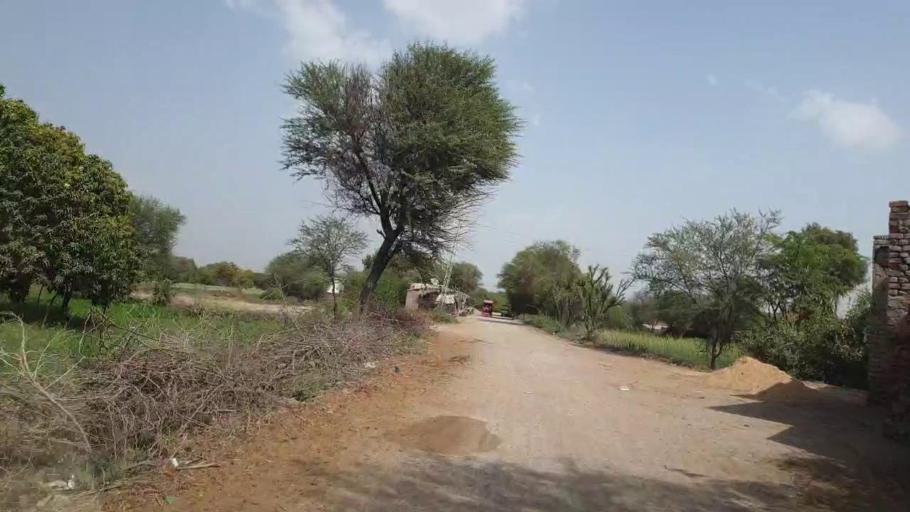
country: PK
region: Sindh
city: Rajo Khanani
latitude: 25.0504
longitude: 68.8636
